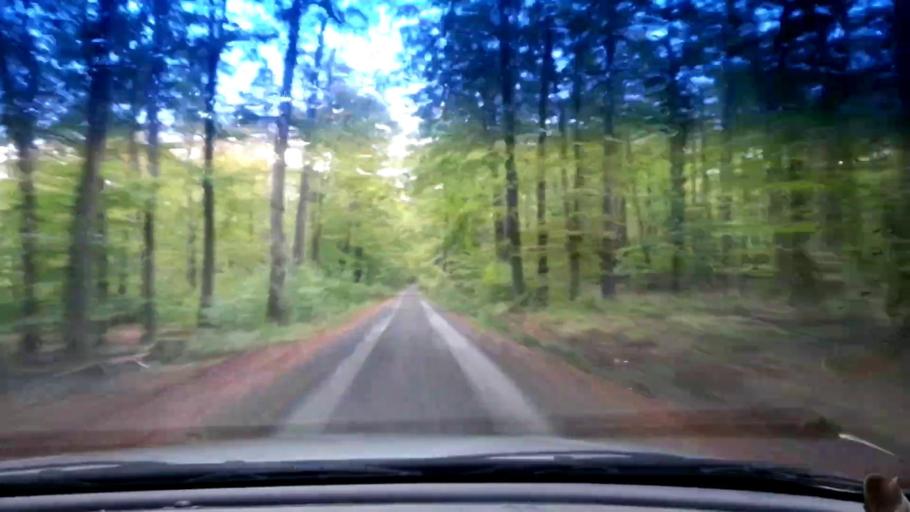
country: DE
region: Bavaria
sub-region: Upper Franconia
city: Burgwindheim
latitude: 49.8501
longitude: 10.6397
